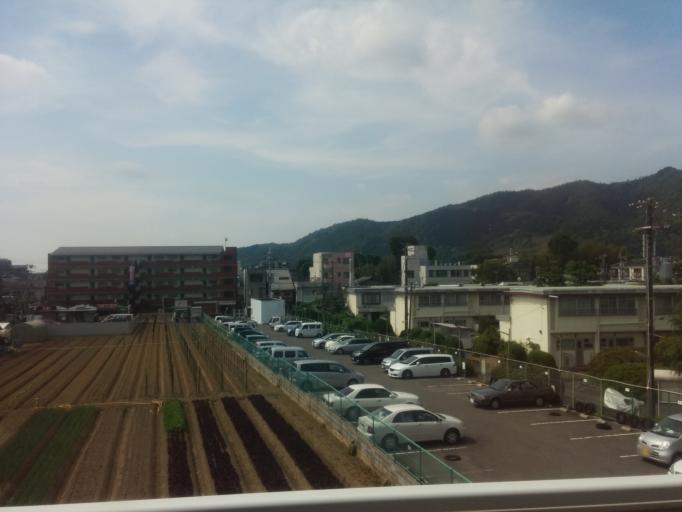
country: JP
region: Kyoto
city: Muko
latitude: 35.0183
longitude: 135.6854
